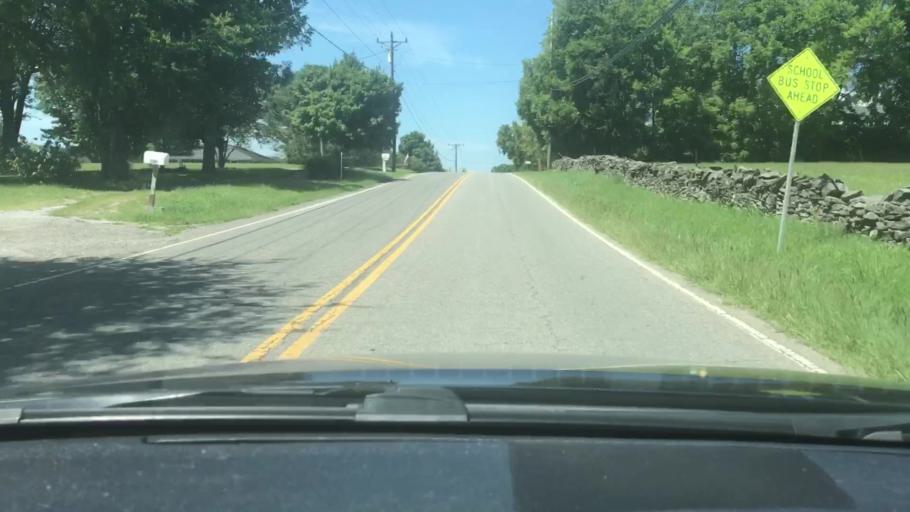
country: US
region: Tennessee
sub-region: Sumner County
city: Gallatin
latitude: 36.4001
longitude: -86.4846
